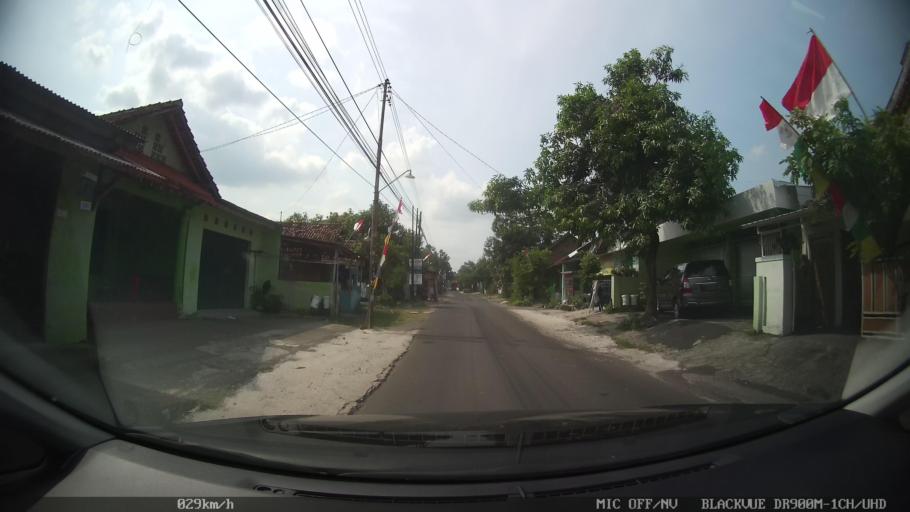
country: ID
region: Daerah Istimewa Yogyakarta
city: Depok
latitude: -7.8014
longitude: 110.4452
